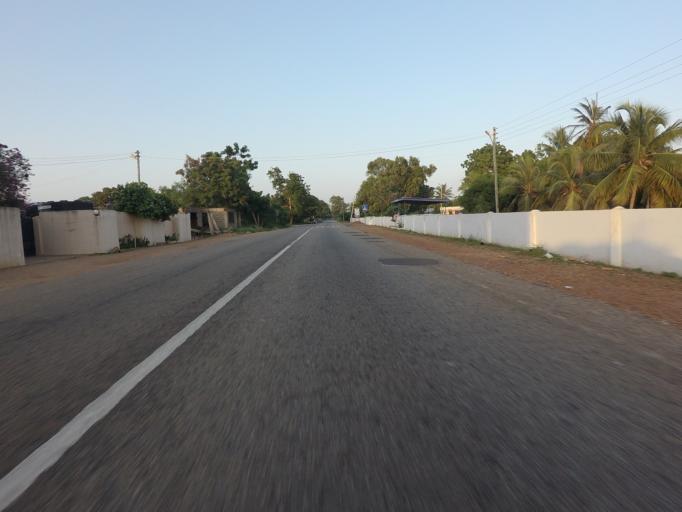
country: GH
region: Volta
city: Anloga
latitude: 5.7902
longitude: 0.8681
